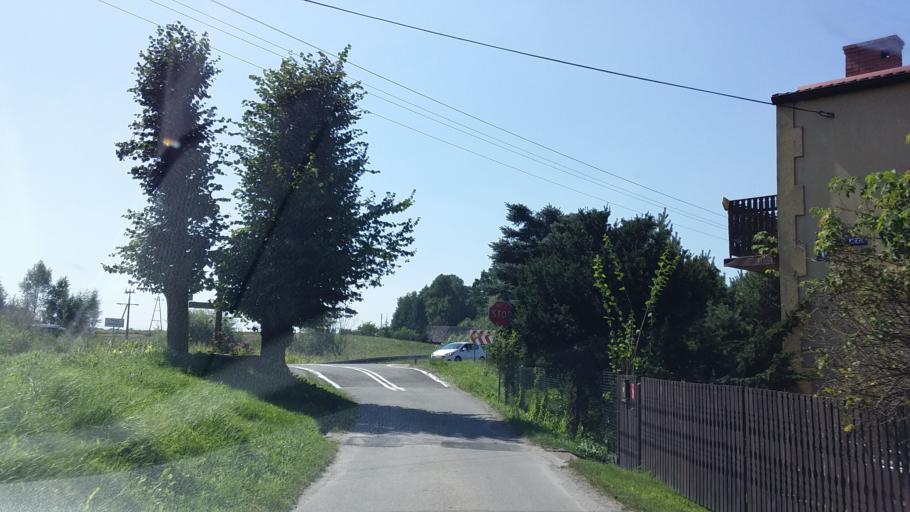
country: PL
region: Lesser Poland Voivodeship
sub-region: Powiat oswiecimski
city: Przeciszow
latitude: 50.0051
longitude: 19.3974
